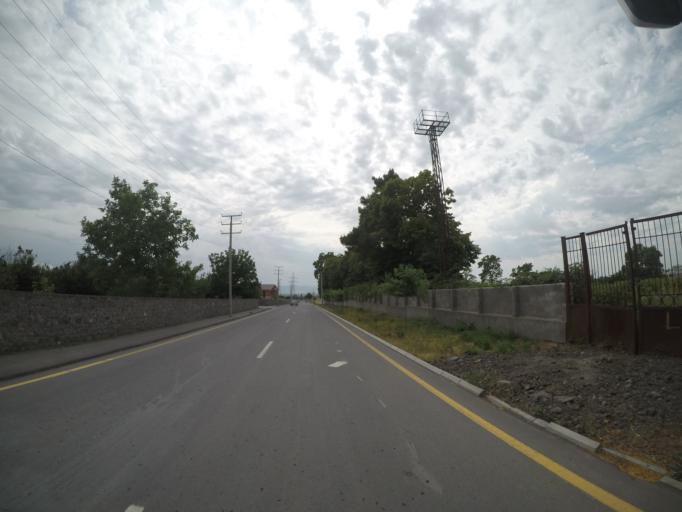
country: AZ
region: Qakh Rayon
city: Qax
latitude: 41.4145
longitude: 46.9035
